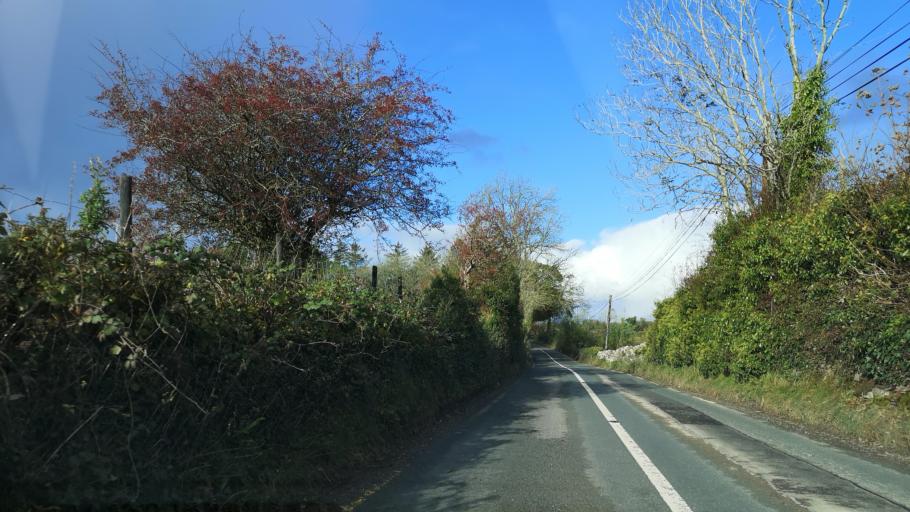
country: IE
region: Connaught
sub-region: Maigh Eo
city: Castlebar
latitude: 53.7709
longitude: -9.3879
